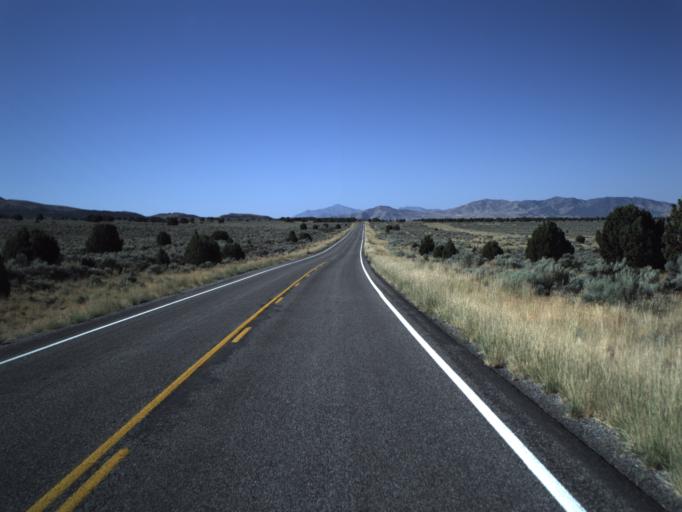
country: US
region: Utah
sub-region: Juab County
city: Mona
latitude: 39.8356
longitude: -112.1384
